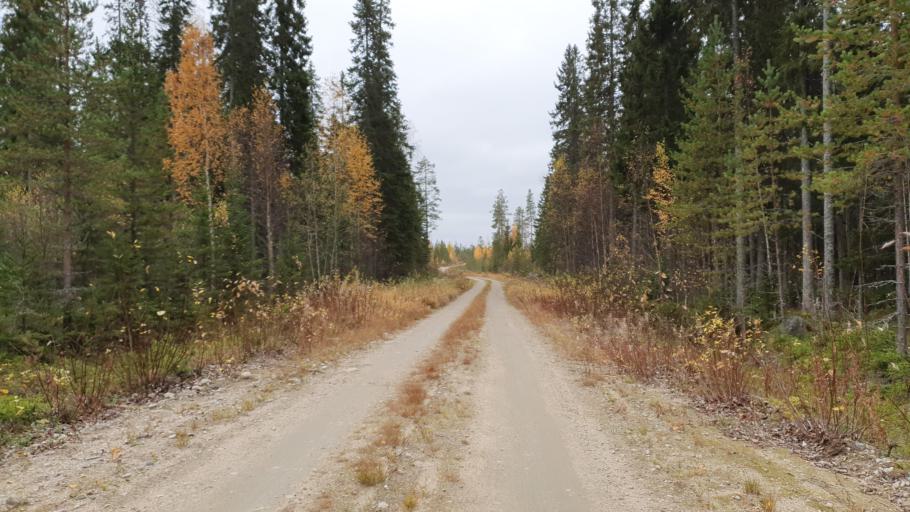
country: FI
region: Kainuu
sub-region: Kehys-Kainuu
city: Kuhmo
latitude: 64.4497
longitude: 29.6086
